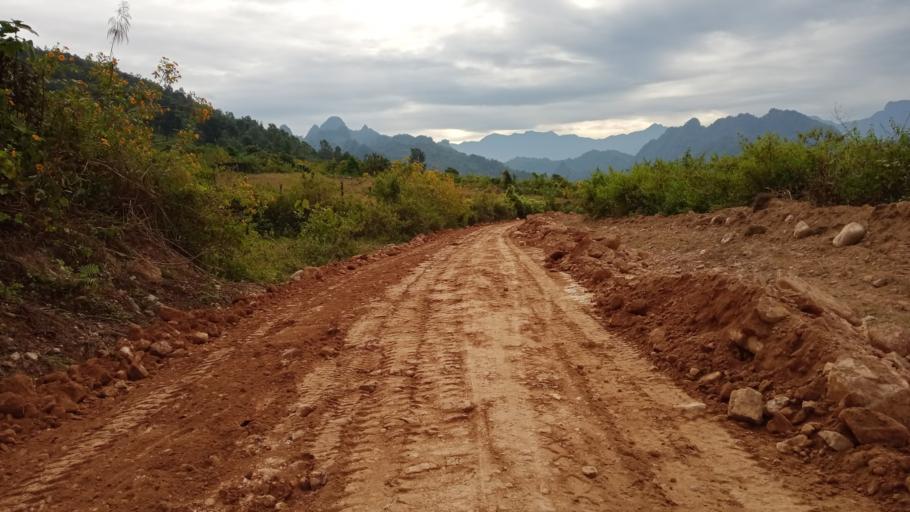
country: LA
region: Xiangkhoang
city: Phonsavan
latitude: 19.1165
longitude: 102.9235
